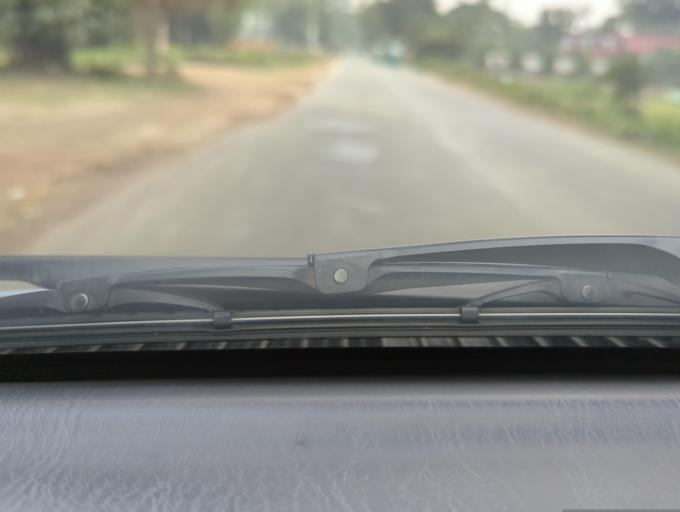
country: BD
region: Sylhet
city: Maulavi Bazar
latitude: 24.5058
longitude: 91.7338
